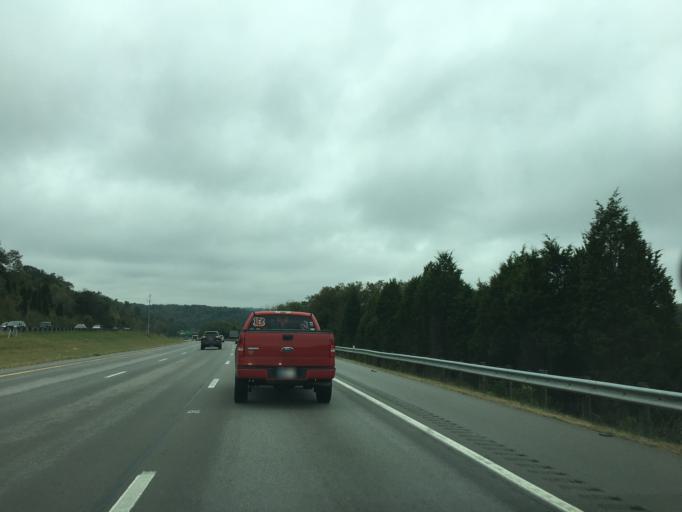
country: US
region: Ohio
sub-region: Hamilton County
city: Dent
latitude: 39.2226
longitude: -84.6638
